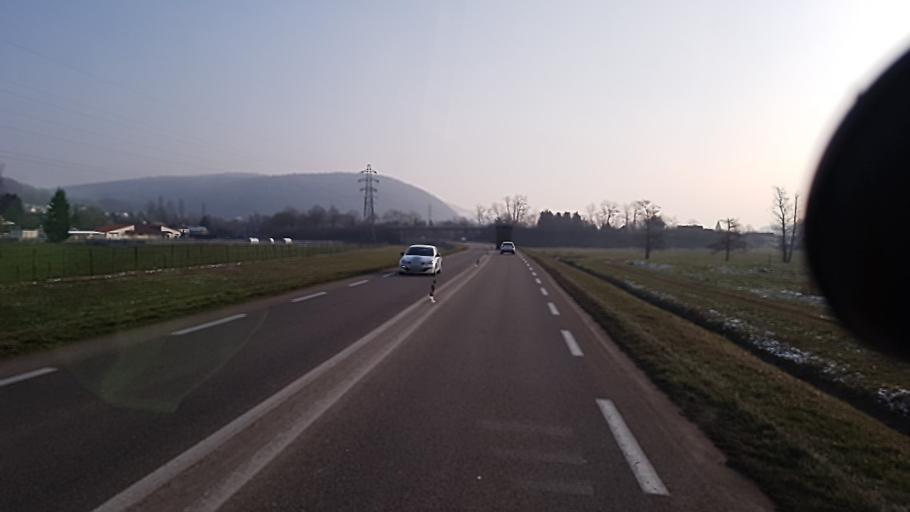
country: FR
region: Alsace
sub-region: Departement du Bas-Rhin
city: Dinsheim-sur-Bruche
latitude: 48.5363
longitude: 7.4193
